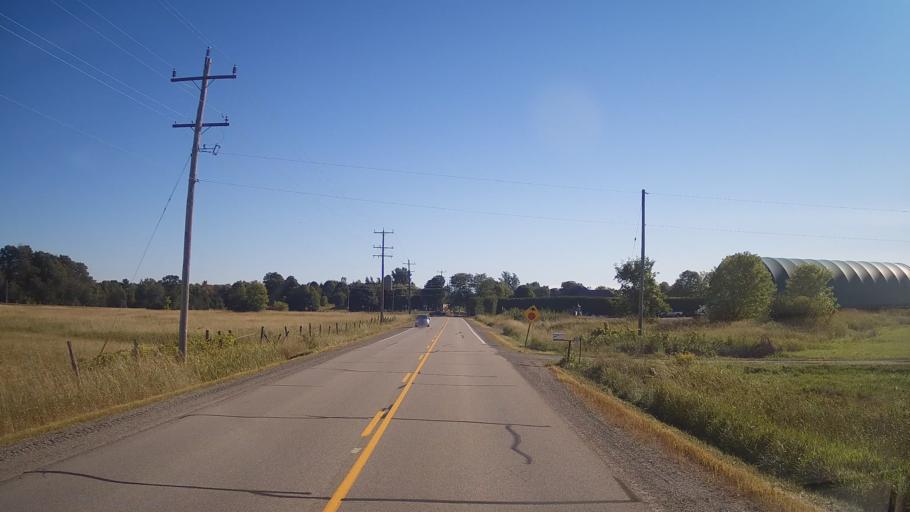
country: CA
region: Ontario
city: Gananoque
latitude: 44.5940
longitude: -76.0920
